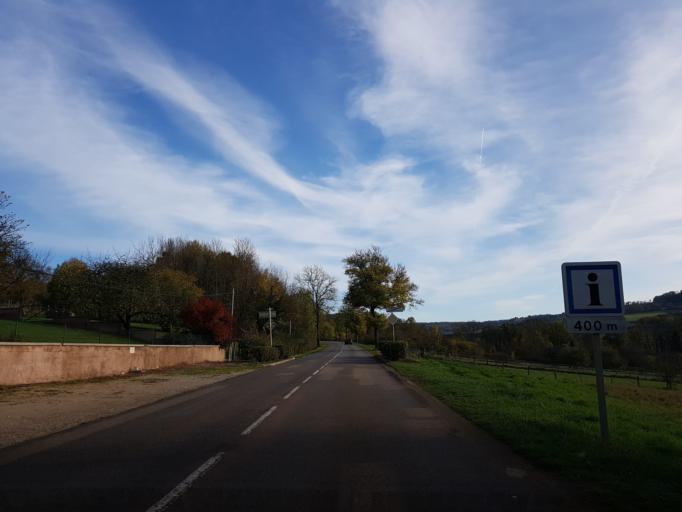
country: FR
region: Bourgogne
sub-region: Departement de la Cote-d'Or
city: Pouilly-en-Auxois
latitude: 47.3174
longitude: 4.6011
